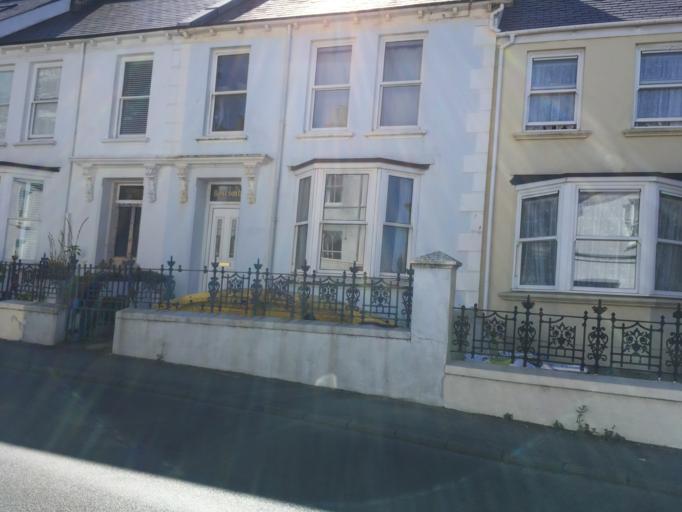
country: GG
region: St Peter Port
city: Saint Peter Port
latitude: 49.4570
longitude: -2.5474
